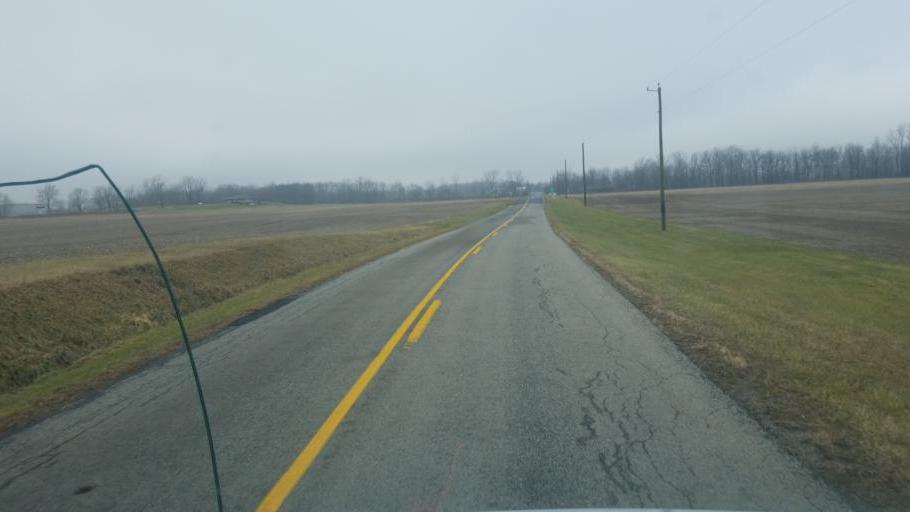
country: US
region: Ohio
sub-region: Champaign County
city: North Lewisburg
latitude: 40.2557
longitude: -83.5473
